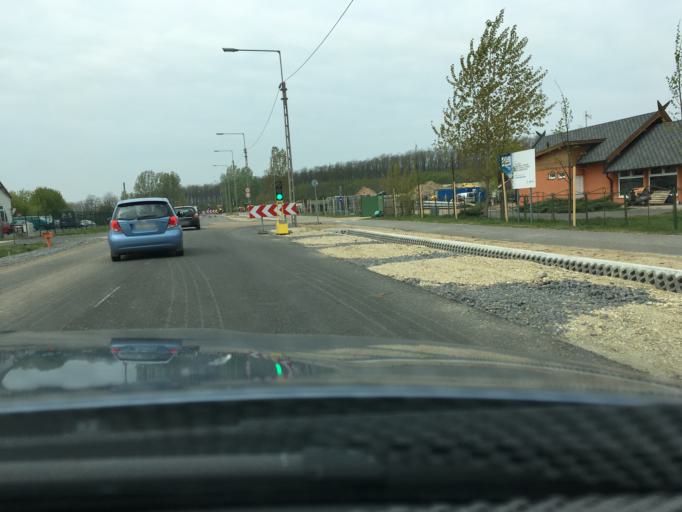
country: HU
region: Hajdu-Bihar
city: Nyiradony
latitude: 47.6834
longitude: 21.8856
